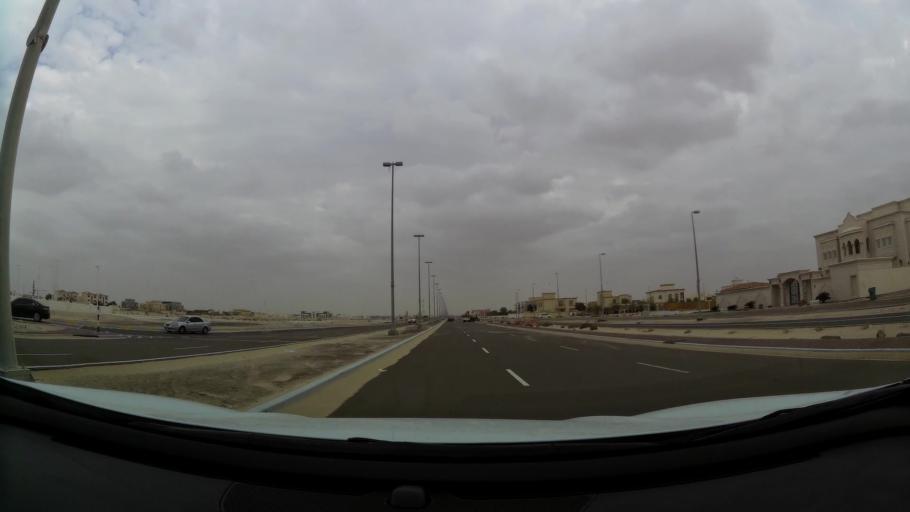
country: AE
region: Abu Dhabi
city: Abu Dhabi
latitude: 24.3676
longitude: 54.6257
